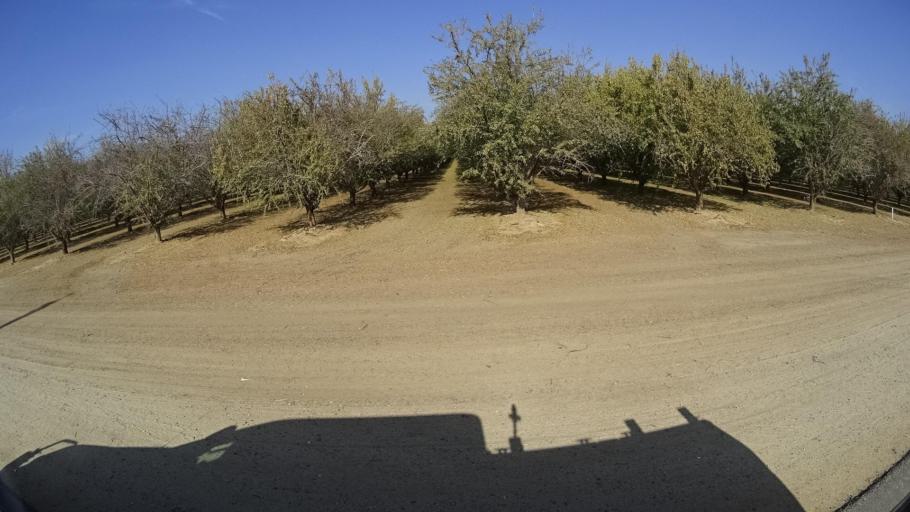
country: US
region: California
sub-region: Kern County
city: Shafter
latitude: 35.5297
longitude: -119.1592
